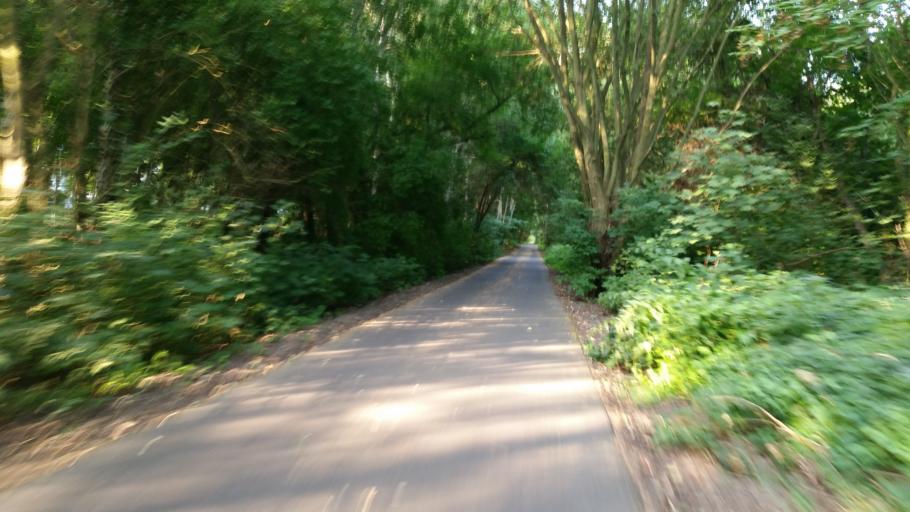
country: DE
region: Brandenburg
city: Teltow
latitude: 52.4105
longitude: 13.2873
